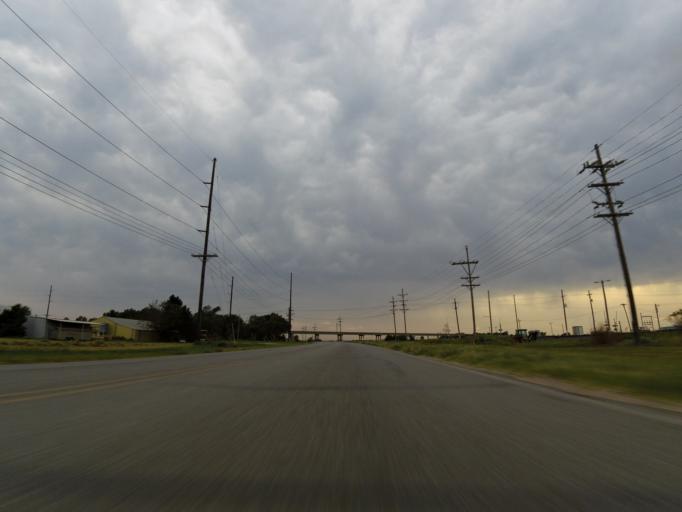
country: US
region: Kansas
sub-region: Reno County
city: South Hutchinson
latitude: 38.0280
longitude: -97.9755
